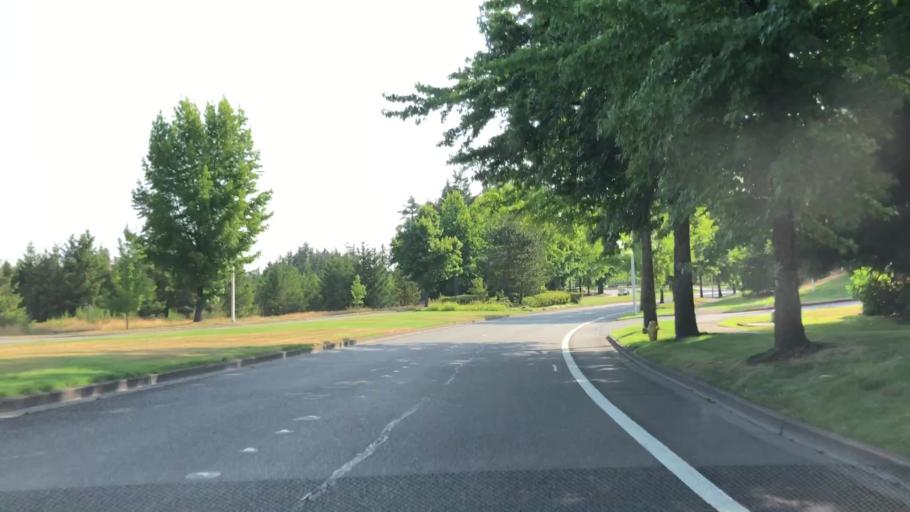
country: US
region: Washington
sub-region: Thurston County
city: Tanglewilde-Thompson Place
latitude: 47.0719
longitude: -122.7552
